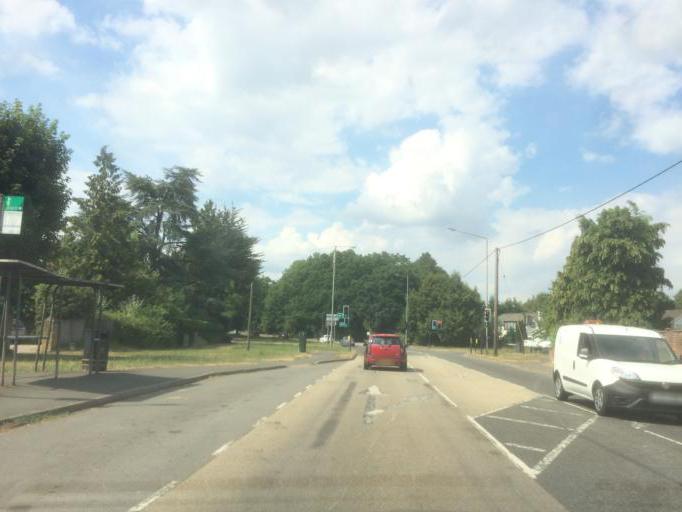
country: GB
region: England
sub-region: Buckinghamshire
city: Farnham Royal
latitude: 51.5630
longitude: -0.6152
